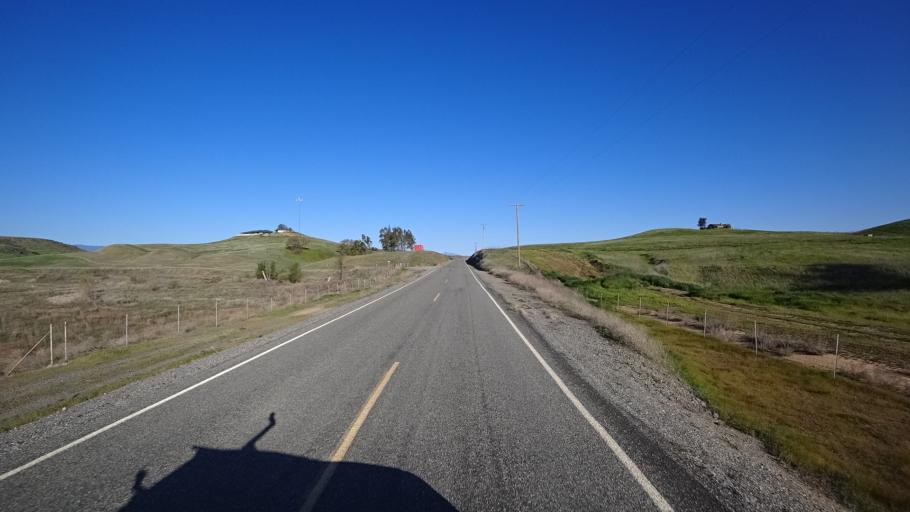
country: US
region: California
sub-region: Glenn County
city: Orland
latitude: 39.8235
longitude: -122.3318
